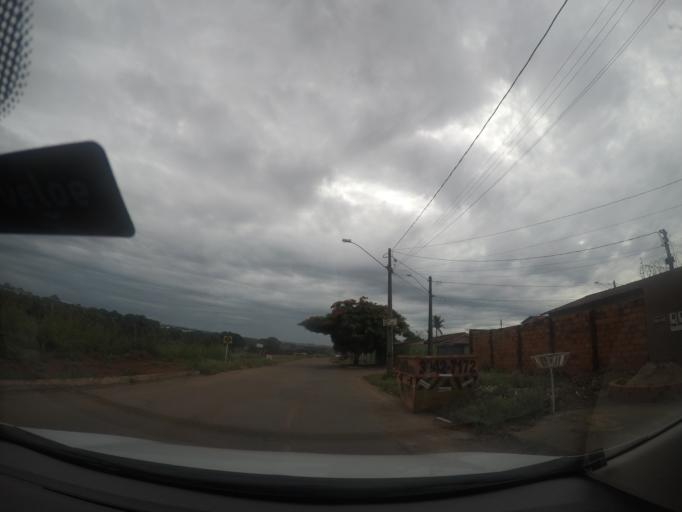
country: BR
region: Goias
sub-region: Goiania
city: Goiania
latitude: -16.6430
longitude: -49.3356
